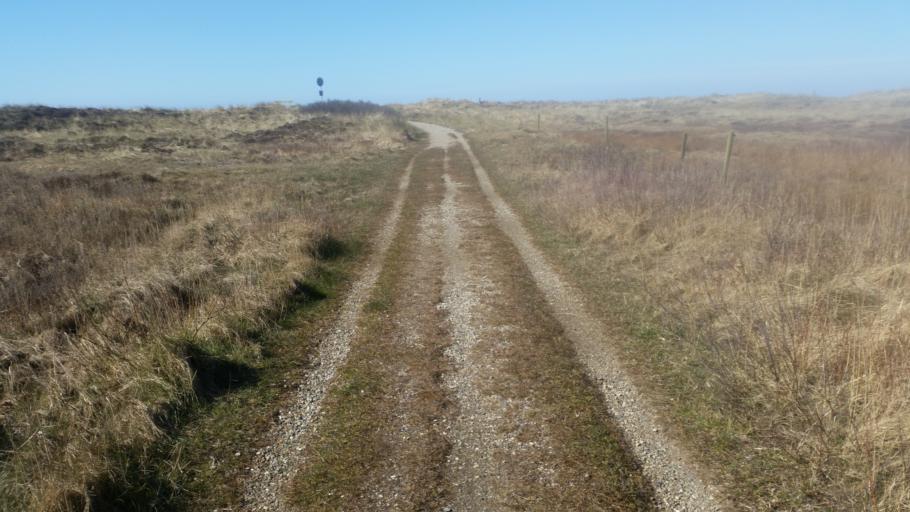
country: DE
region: Schleswig-Holstein
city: List
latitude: 55.1545
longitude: 8.5003
